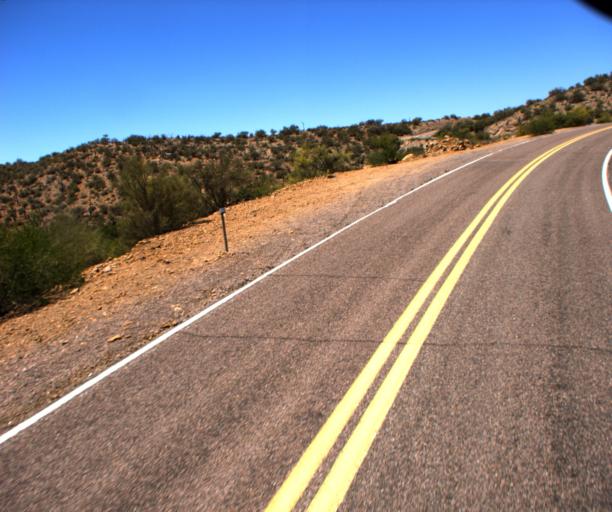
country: US
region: Arizona
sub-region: Yavapai County
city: Bagdad
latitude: 34.4550
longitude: -112.9959
